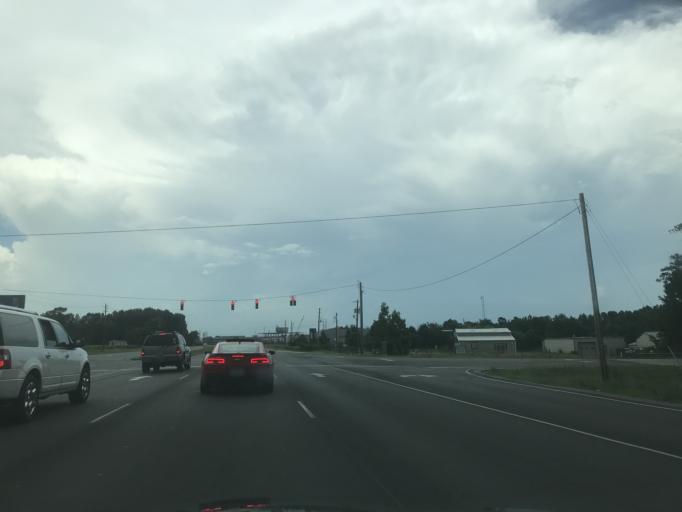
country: US
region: North Carolina
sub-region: Johnston County
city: Clayton
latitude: 35.6083
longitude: -78.4164
